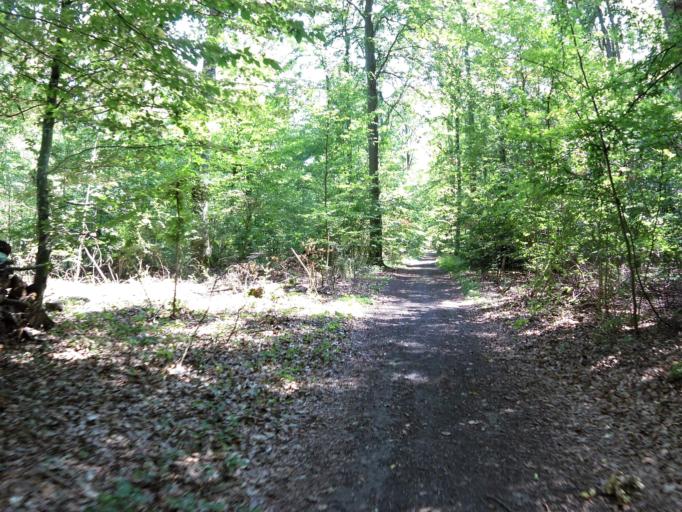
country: DE
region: Bavaria
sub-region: Regierungsbezirk Unterfranken
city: Gadheim
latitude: 49.8522
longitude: 9.8924
